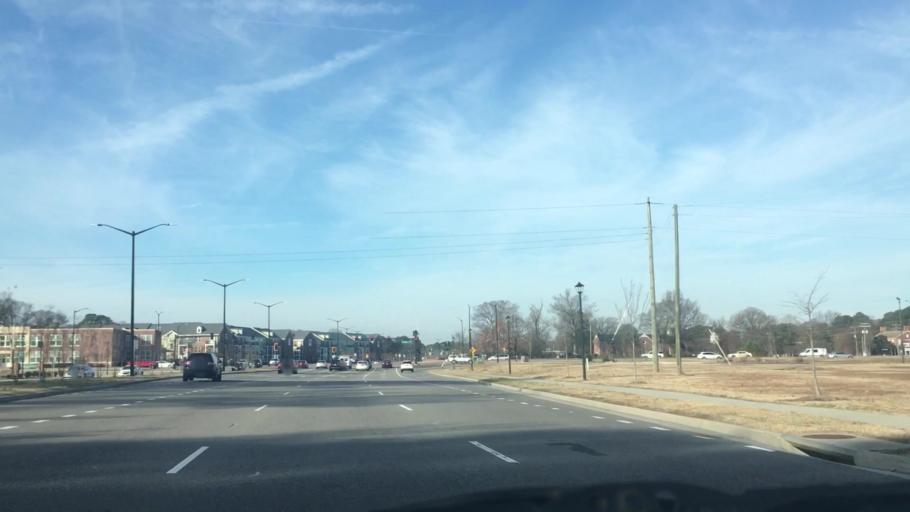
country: US
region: Virginia
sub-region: City of Chesapeake
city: Chesapeake
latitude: 36.8252
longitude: -76.1588
